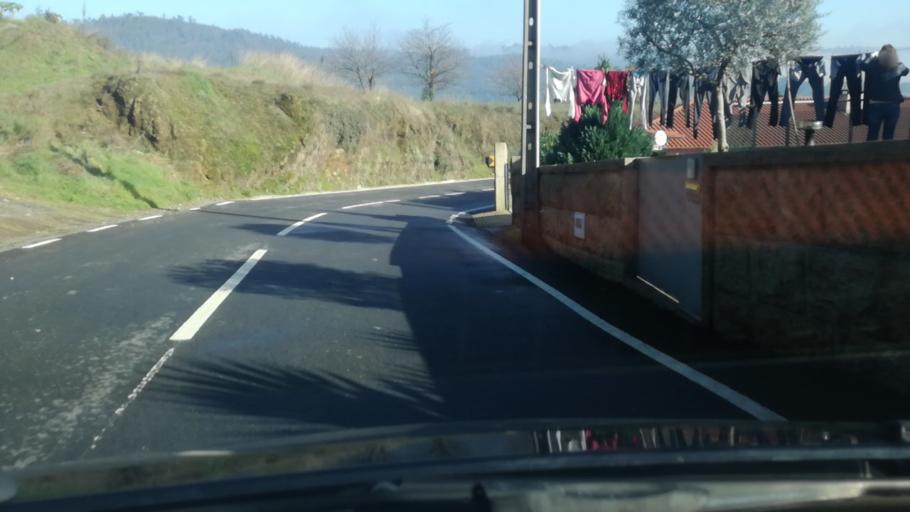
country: PT
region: Braga
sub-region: Guimaraes
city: Ponte
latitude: 41.5275
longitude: -8.3431
